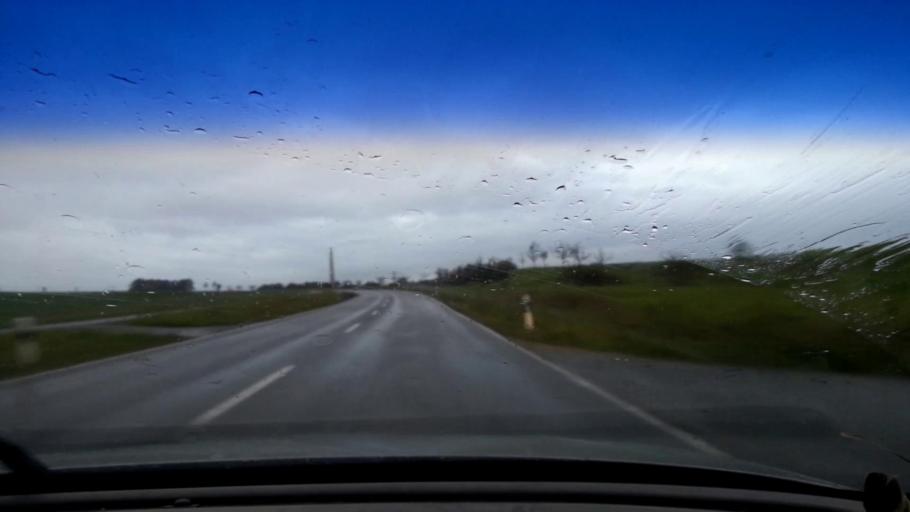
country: DE
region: Bavaria
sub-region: Upper Franconia
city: Walsdorf
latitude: 49.8796
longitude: 10.7836
